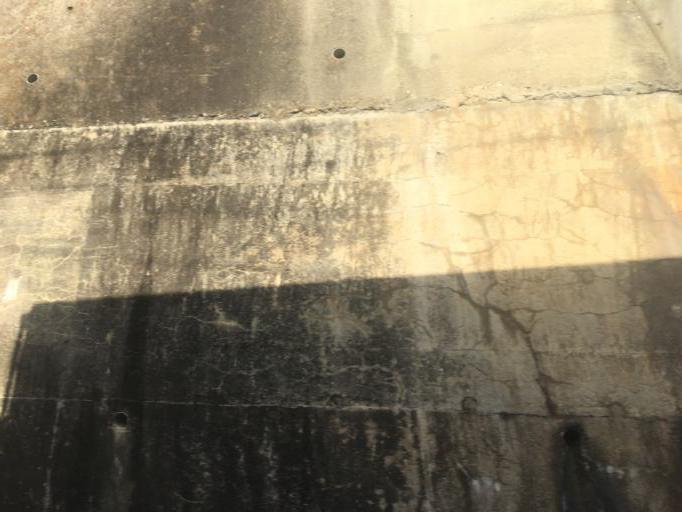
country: JP
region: Fukushima
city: Hobaramachi
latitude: 37.8203
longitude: 140.5674
